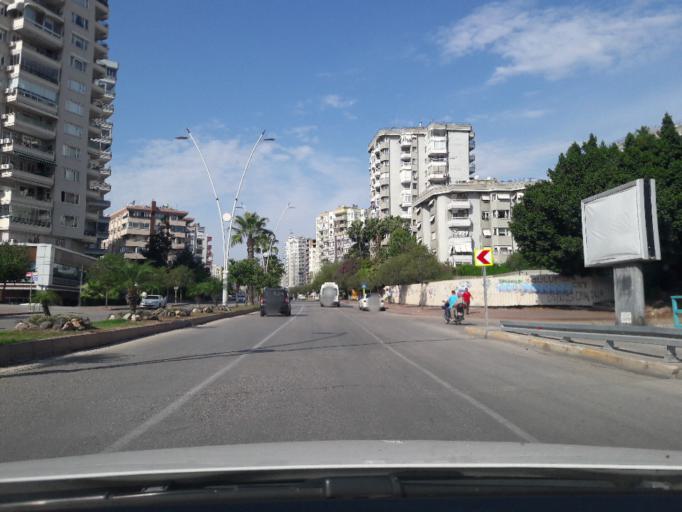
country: TR
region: Adana
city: Adana
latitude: 37.0148
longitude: 35.3261
